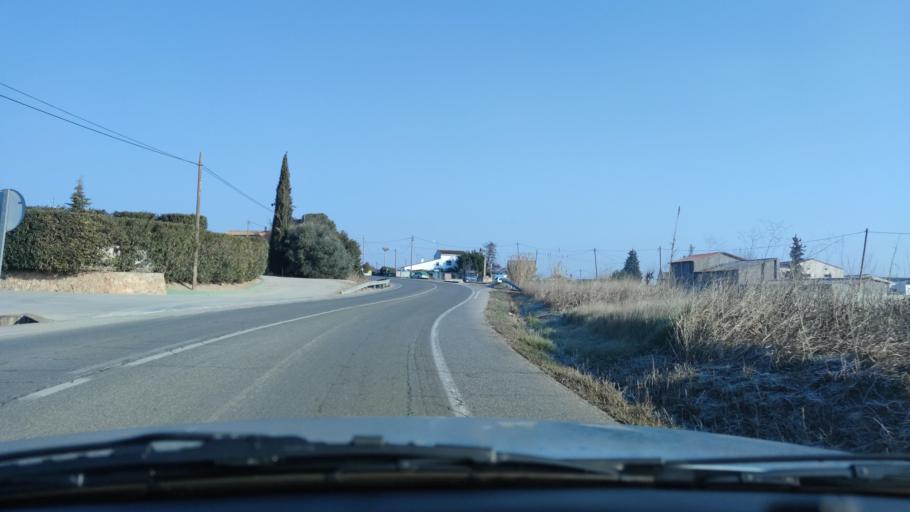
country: ES
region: Catalonia
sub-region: Provincia de Lleida
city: Lleida
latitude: 41.6384
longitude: 0.6370
